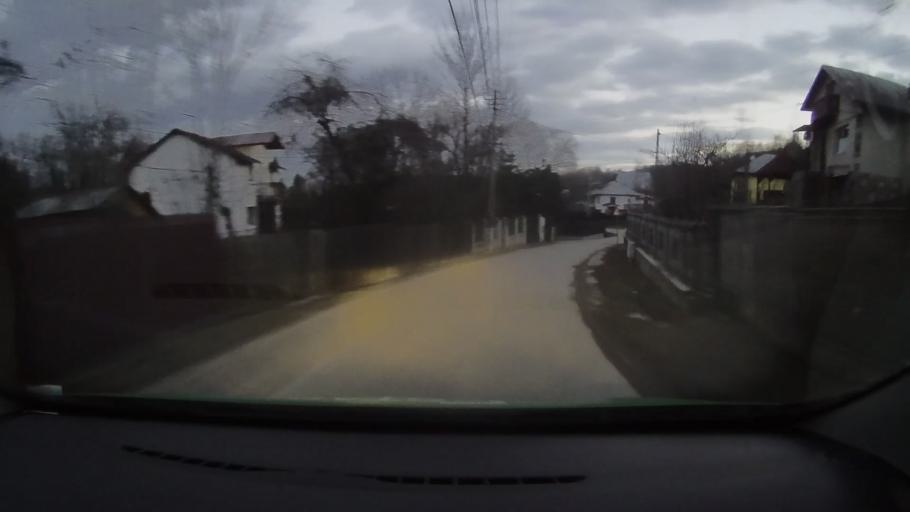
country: RO
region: Prahova
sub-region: Comuna Provita de Sus
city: Provita de Sus
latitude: 45.1393
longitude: 25.6308
